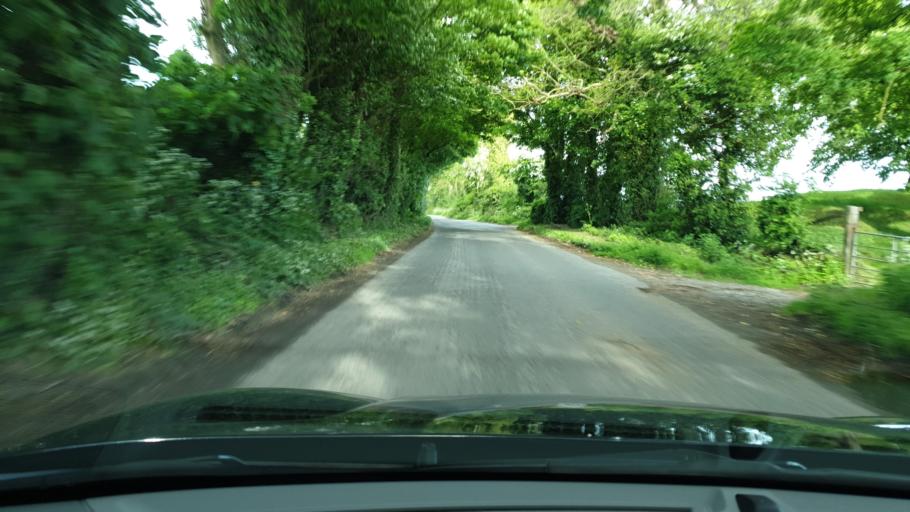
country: IE
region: Leinster
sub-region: An Mhi
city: Stamullin
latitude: 53.5566
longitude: -6.3043
